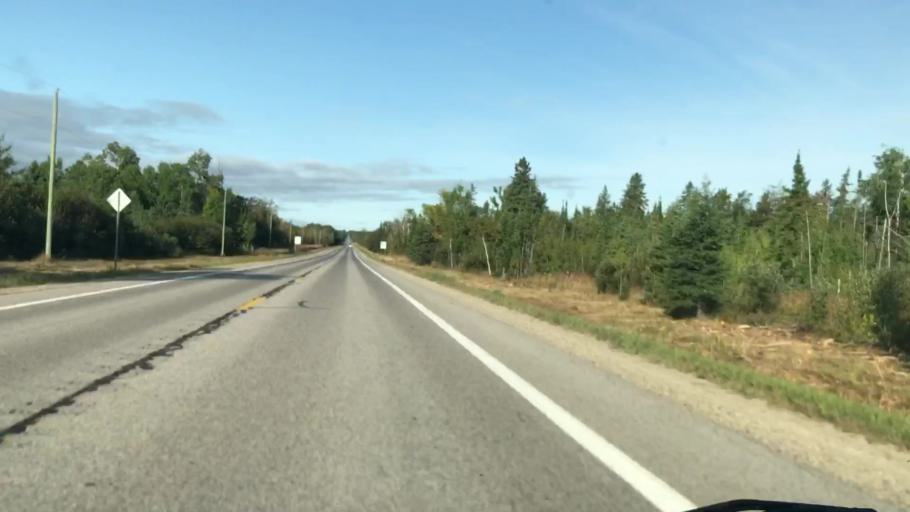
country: US
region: Michigan
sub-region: Luce County
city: Newberry
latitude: 46.3035
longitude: -85.3769
